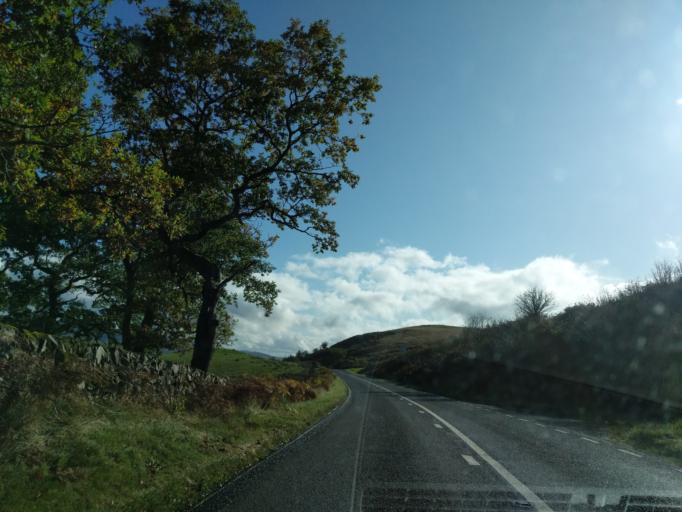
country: GB
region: Scotland
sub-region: Dumfries and Galloway
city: Moffat
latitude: 55.3630
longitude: -3.4783
